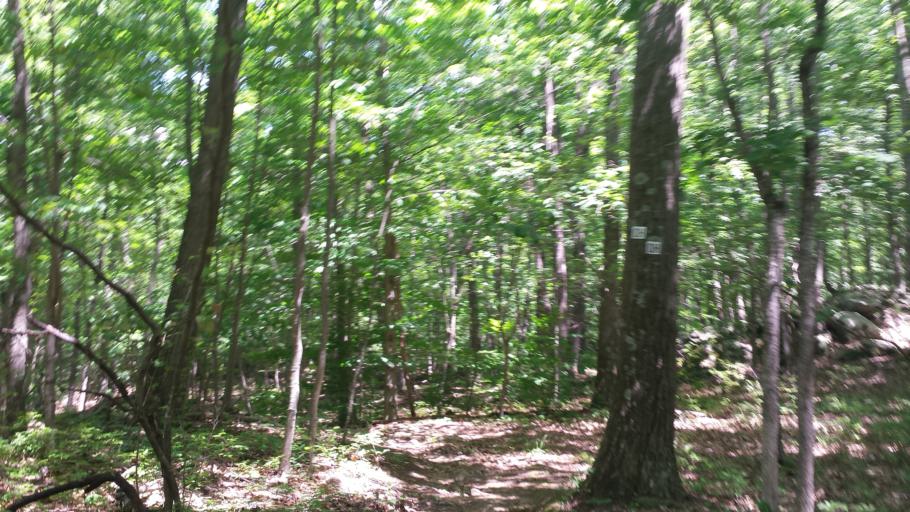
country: US
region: New York
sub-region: Westchester County
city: Pound Ridge
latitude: 41.2663
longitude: -73.5731
